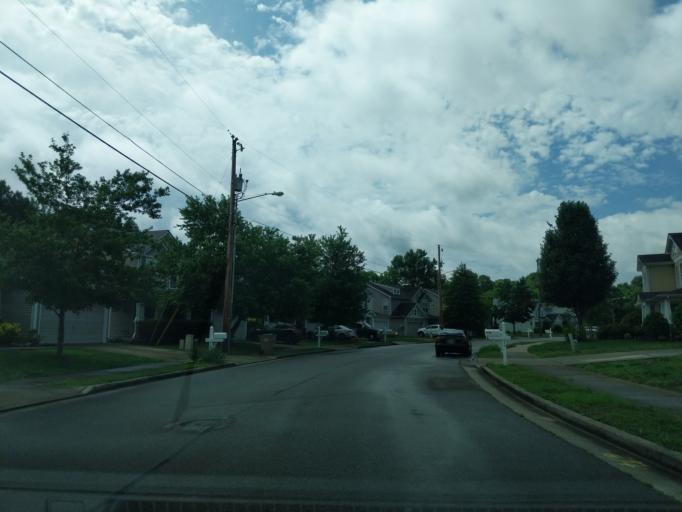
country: US
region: Tennessee
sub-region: Davidson County
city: Lakewood
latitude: 36.2355
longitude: -86.6915
